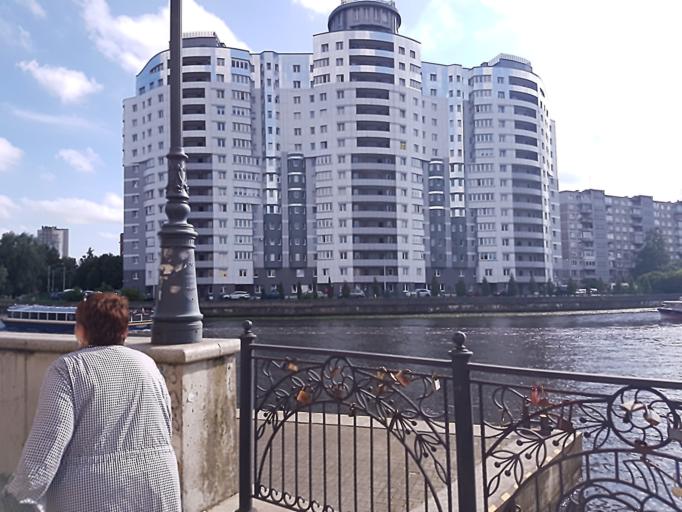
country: RU
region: Kaliningrad
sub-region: Gorod Kaliningrad
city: Kaliningrad
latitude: 54.7052
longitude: 20.5144
